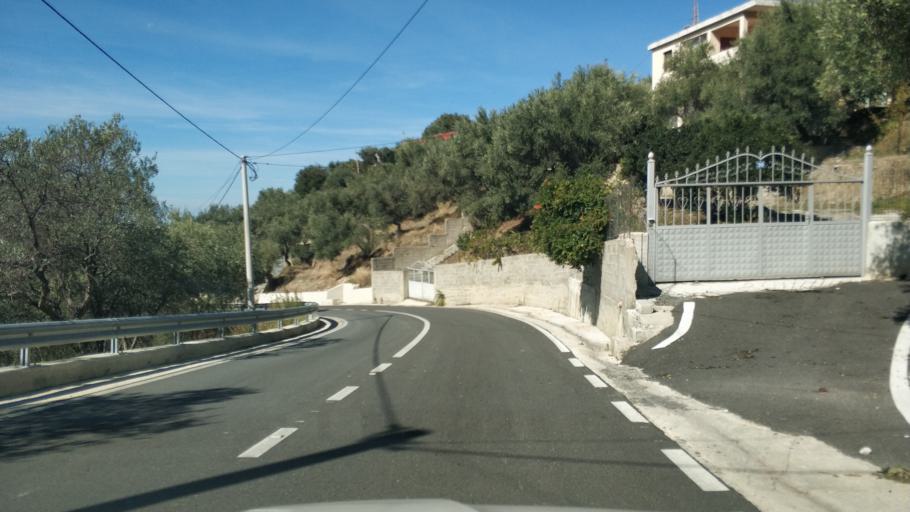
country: AL
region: Vlore
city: Vlore
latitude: 40.4569
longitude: 19.5025
